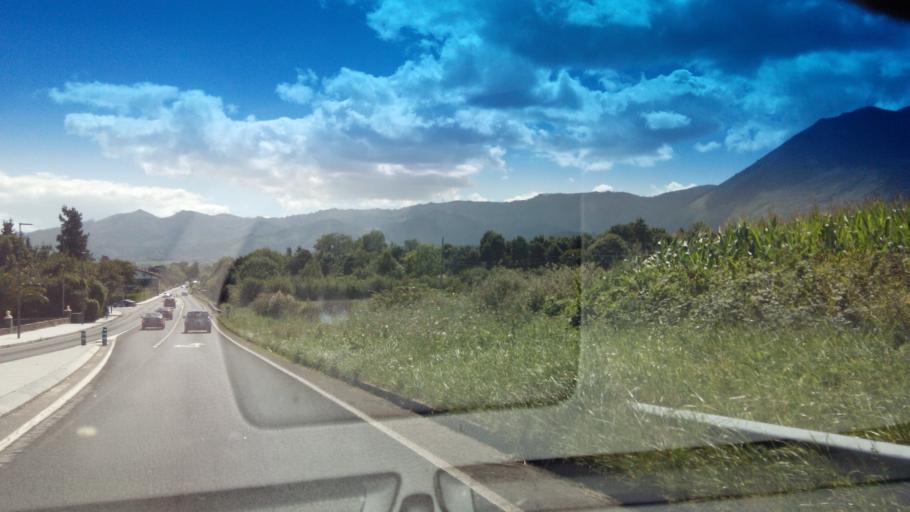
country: ES
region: Asturias
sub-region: Province of Asturias
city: Colunga
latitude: 43.4807
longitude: -5.2328
